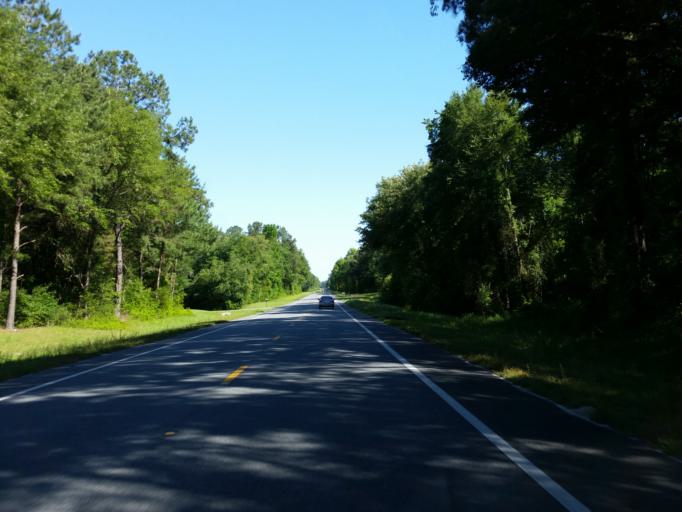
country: US
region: Florida
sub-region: Hamilton County
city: Jasper
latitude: 30.5711
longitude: -83.0790
